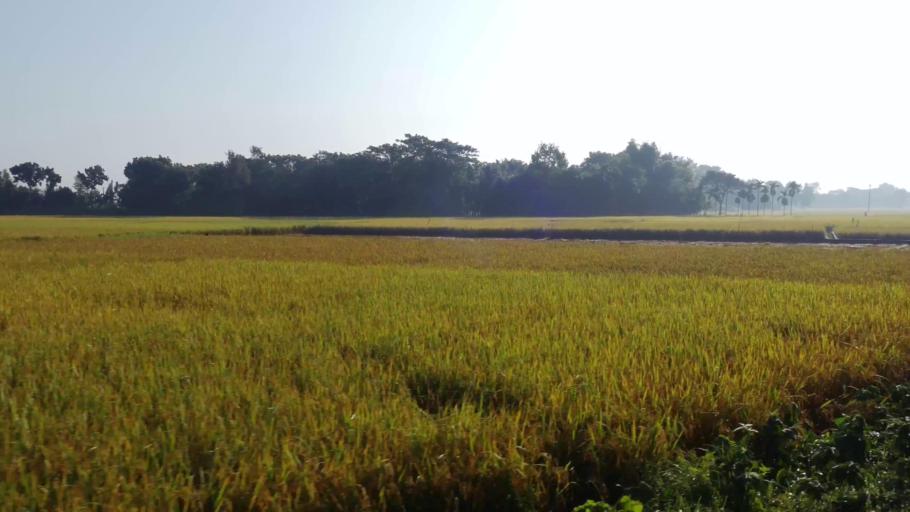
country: BD
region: Dhaka
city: Jamalpur
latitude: 24.8632
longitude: 90.0714
